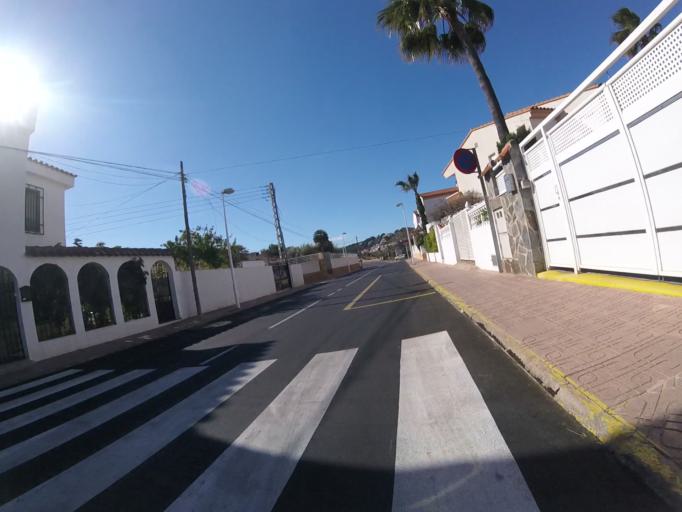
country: ES
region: Valencia
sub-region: Provincia de Castello
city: Orpesa/Oropesa del Mar
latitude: 40.0914
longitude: 0.1313
